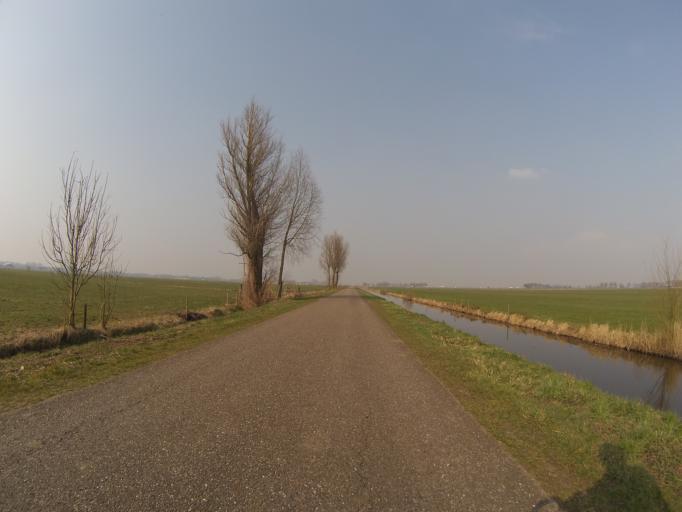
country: NL
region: Utrecht
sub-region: Gemeente Baarn
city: Baarn
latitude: 52.2038
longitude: 5.3304
